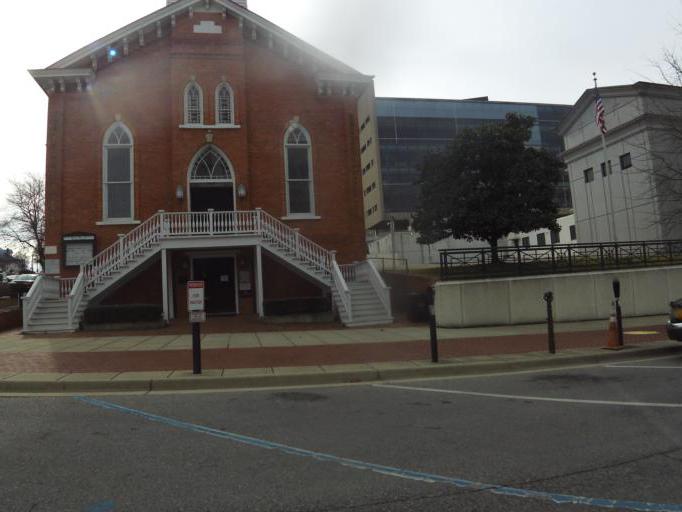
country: US
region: Alabama
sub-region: Montgomery County
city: Montgomery
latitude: 32.3776
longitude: -86.3027
